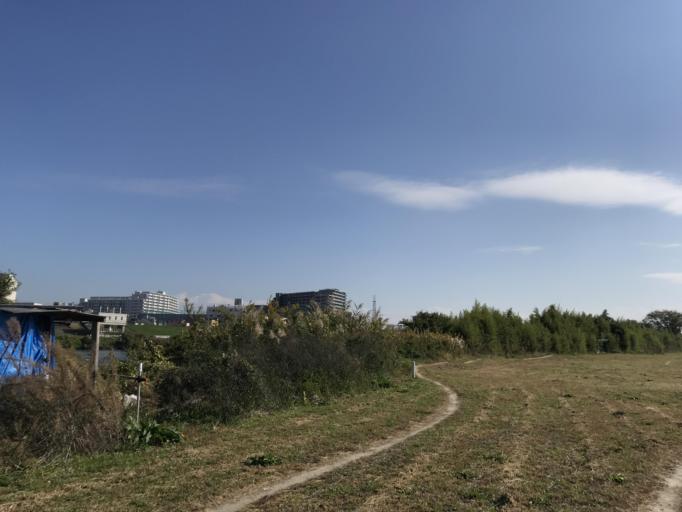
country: JP
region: Kanagawa
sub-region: Kawasaki-shi
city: Kawasaki
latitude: 35.5585
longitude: 139.6866
